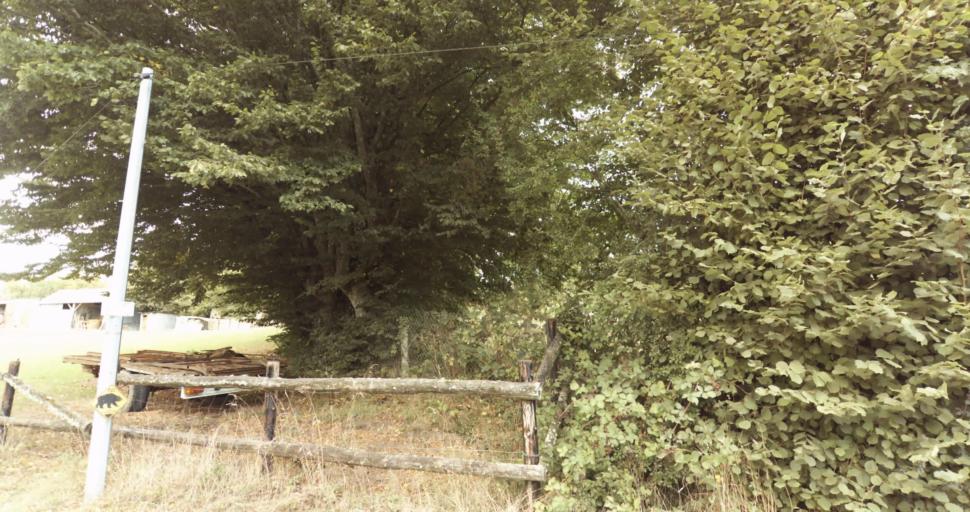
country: FR
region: Lower Normandy
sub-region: Departement de l'Orne
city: Sainte-Gauburge-Sainte-Colombe
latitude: 48.7259
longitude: 0.4293
